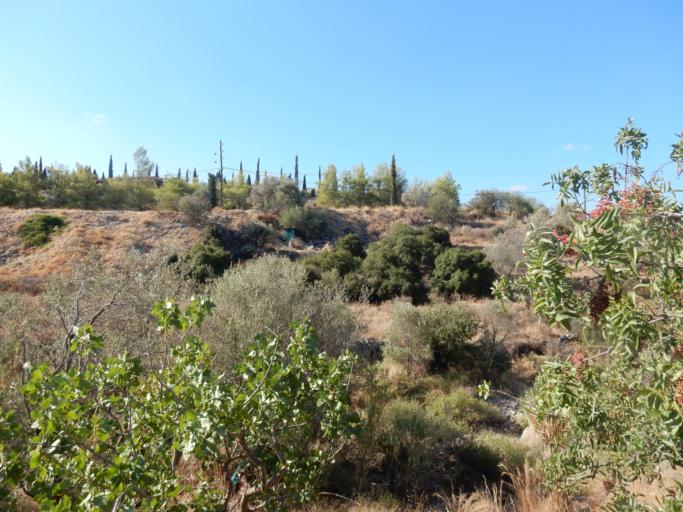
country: GR
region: Attica
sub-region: Nomos Piraios
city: Kypseli
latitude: 37.7347
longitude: 23.4560
